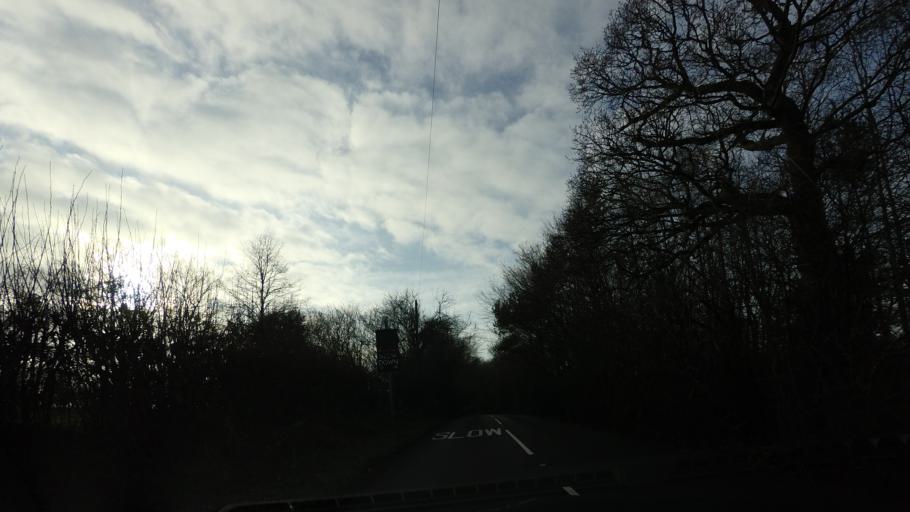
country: GB
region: England
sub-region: East Sussex
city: Battle
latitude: 50.9061
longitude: 0.4807
